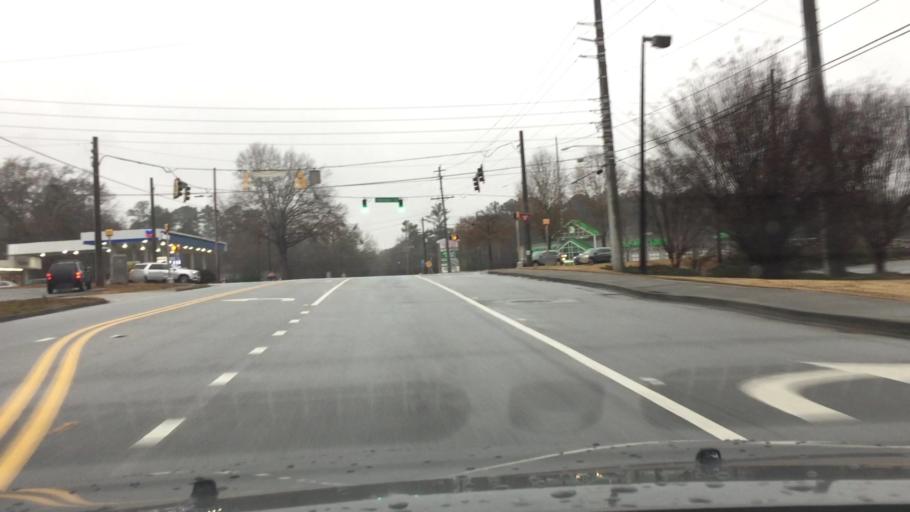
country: US
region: Georgia
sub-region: Cobb County
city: Powder Springs
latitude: 33.8727
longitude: -84.6761
